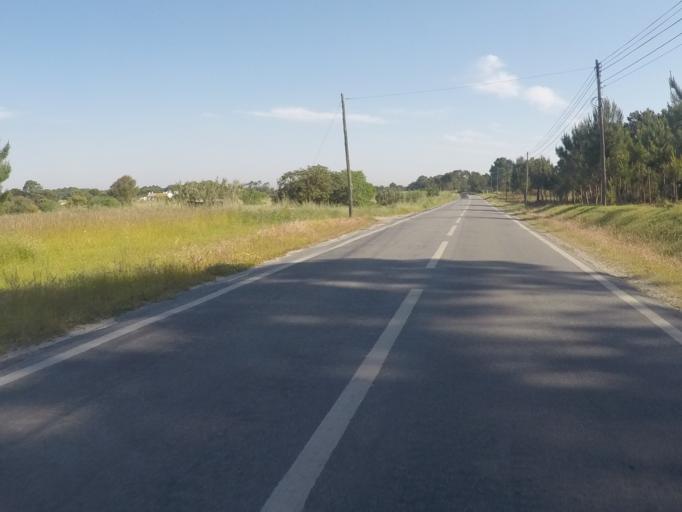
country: PT
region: Setubal
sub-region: Sesimbra
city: Sesimbra
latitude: 38.4903
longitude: -9.1573
